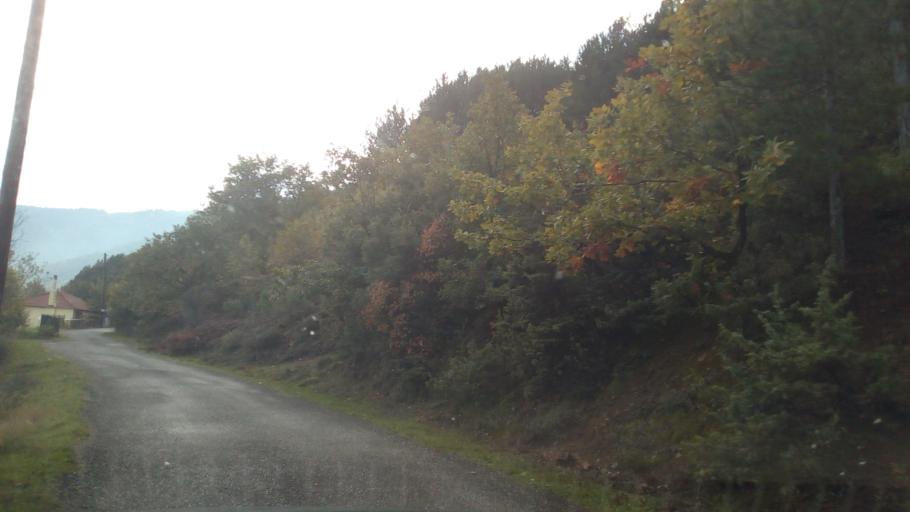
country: GR
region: Central Greece
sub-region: Nomos Fokidos
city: Lidoriki
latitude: 38.4912
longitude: 22.0510
